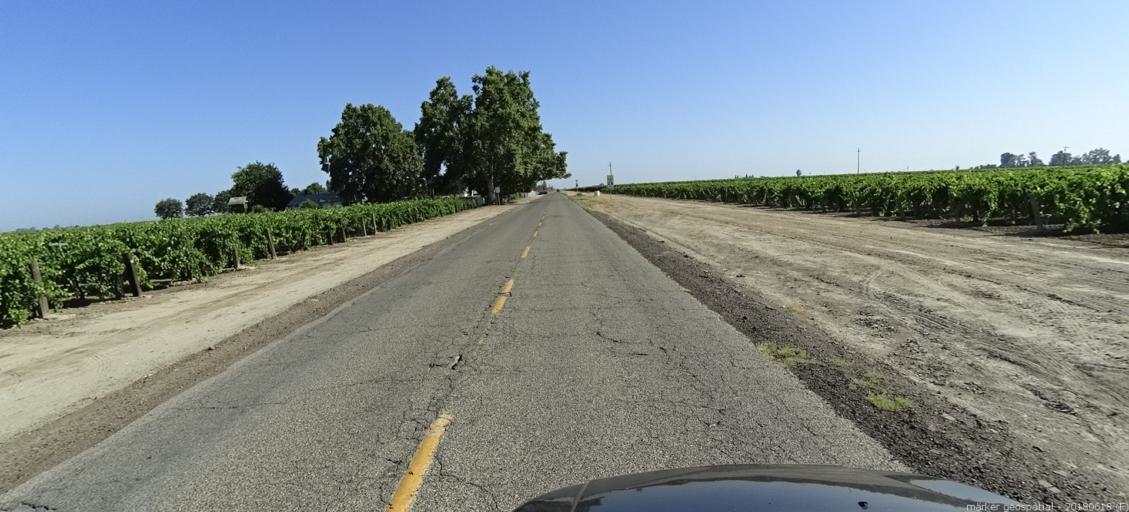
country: US
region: California
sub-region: Madera County
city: Parkwood
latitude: 36.8712
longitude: -120.1284
